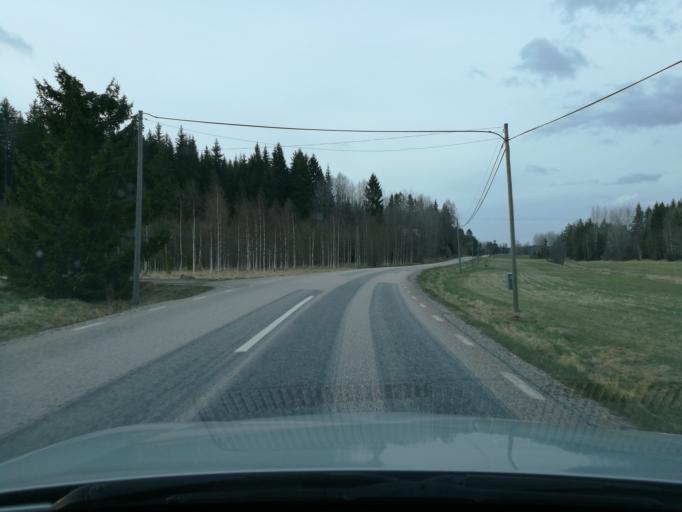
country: SE
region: Soedermanland
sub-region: Gnesta Kommun
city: Gnesta
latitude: 58.9556
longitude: 17.3504
